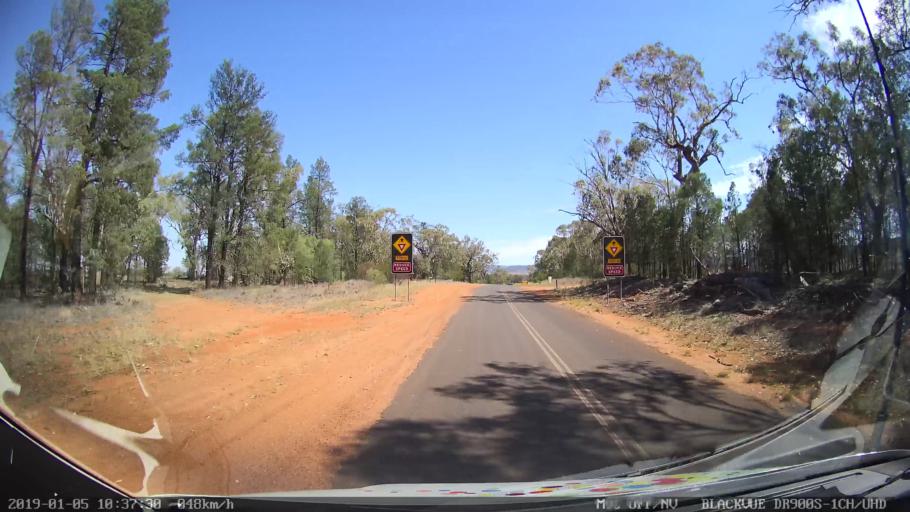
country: AU
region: New South Wales
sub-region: Gilgandra
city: Gilgandra
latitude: -31.4741
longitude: 148.9213
